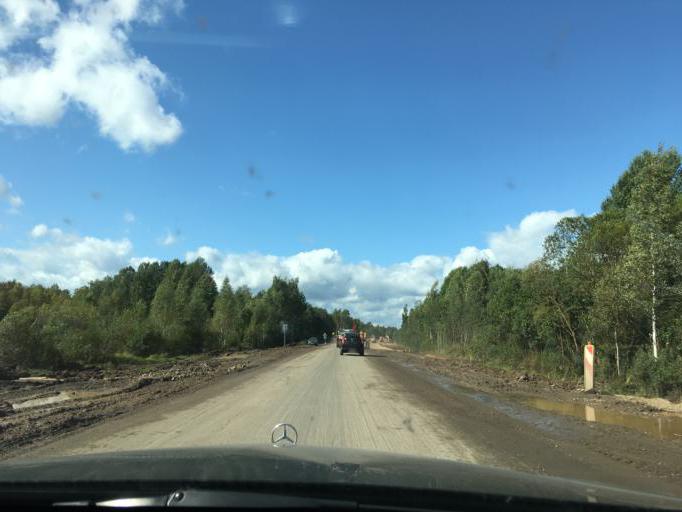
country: RU
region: Pskov
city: Velikiye Luki
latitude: 56.2719
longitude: 30.3518
